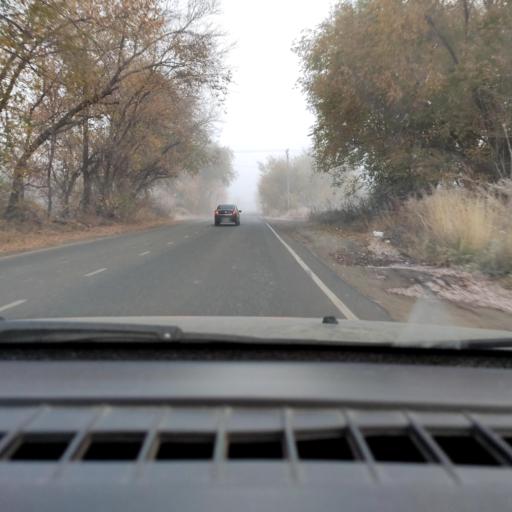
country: RU
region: Samara
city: Tol'yatti
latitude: 53.5835
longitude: 49.2568
